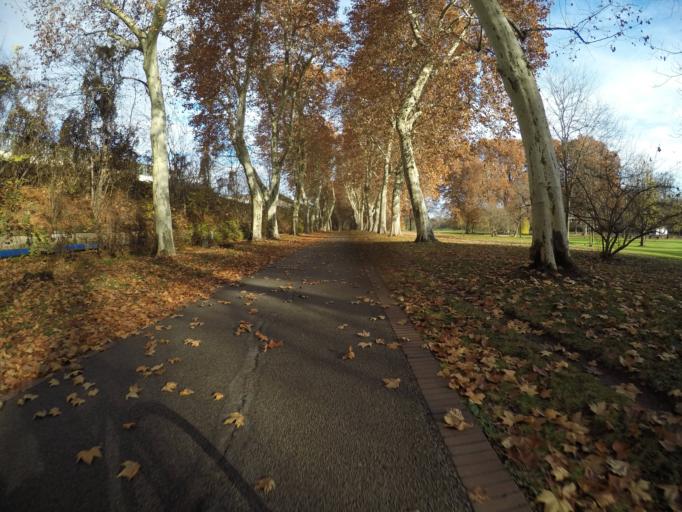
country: DE
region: Baden-Wuerttemberg
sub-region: Regierungsbezirk Stuttgart
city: Stuttgart-Ost
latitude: 48.7938
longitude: 9.1961
